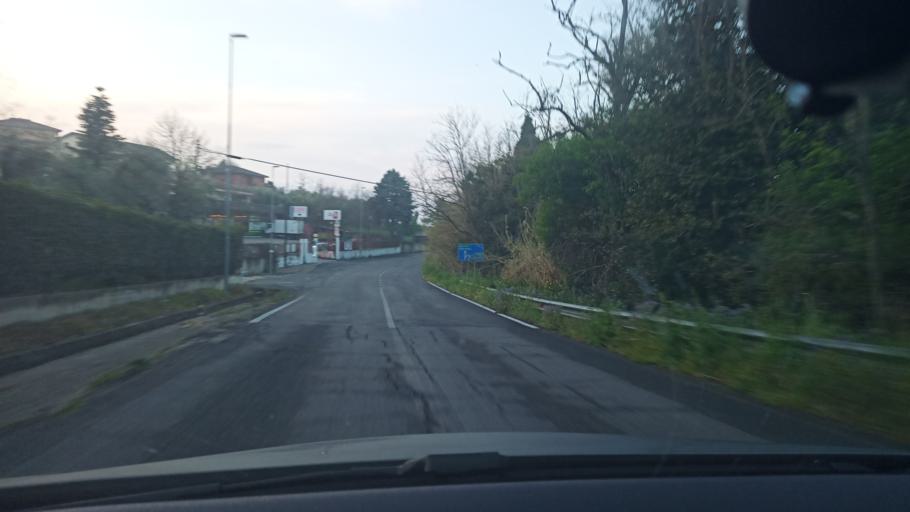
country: IT
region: Latium
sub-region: Provincia di Rieti
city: Cantalupo in Sabina
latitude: 42.3033
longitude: 12.6461
